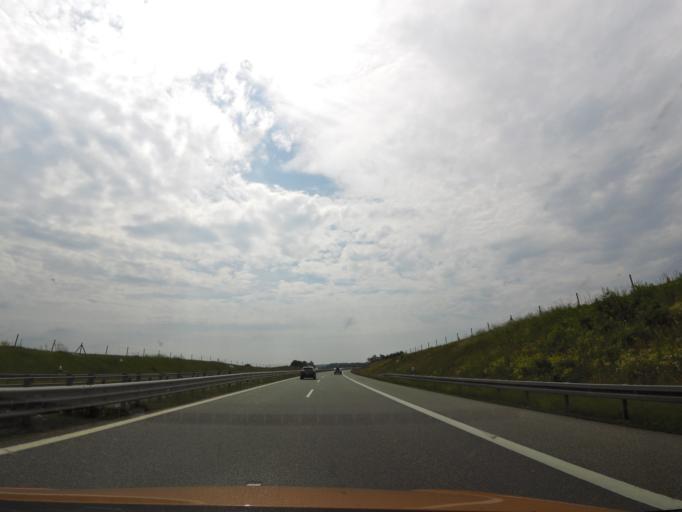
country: DE
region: Mecklenburg-Vorpommern
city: Retgendorf
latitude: 53.7390
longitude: 11.5790
